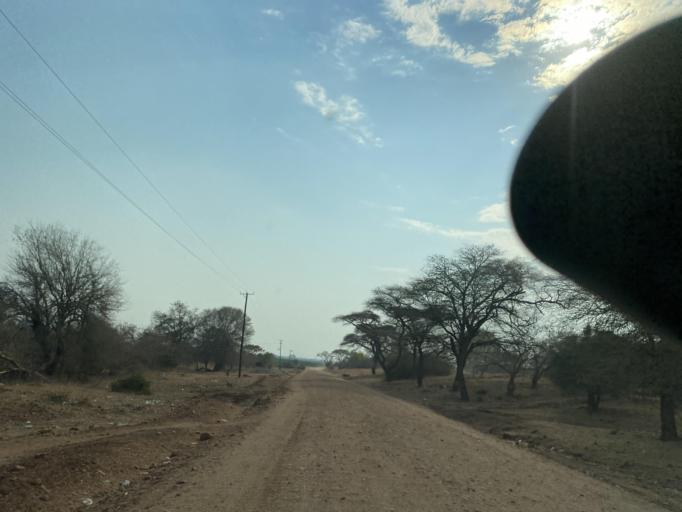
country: ZW
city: Chirundu
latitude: -15.9291
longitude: 28.9676
